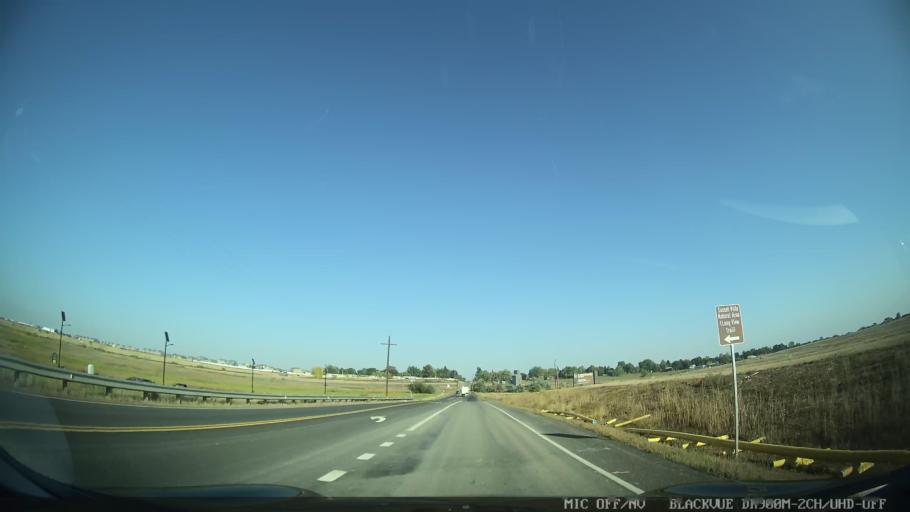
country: US
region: Colorado
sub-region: Larimer County
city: Loveland
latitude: 40.4510
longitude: -105.0934
